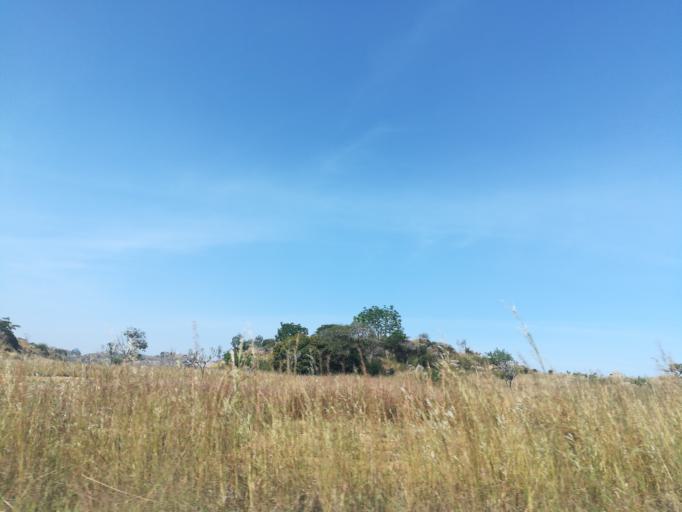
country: NG
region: Plateau
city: Bukuru
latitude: 9.7572
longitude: 8.9077
